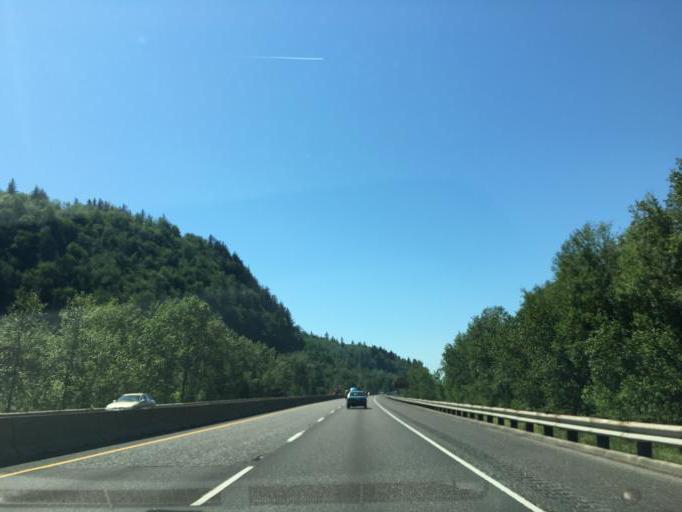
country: US
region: Washington
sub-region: Clark County
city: Washougal
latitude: 45.5418
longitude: -122.2574
